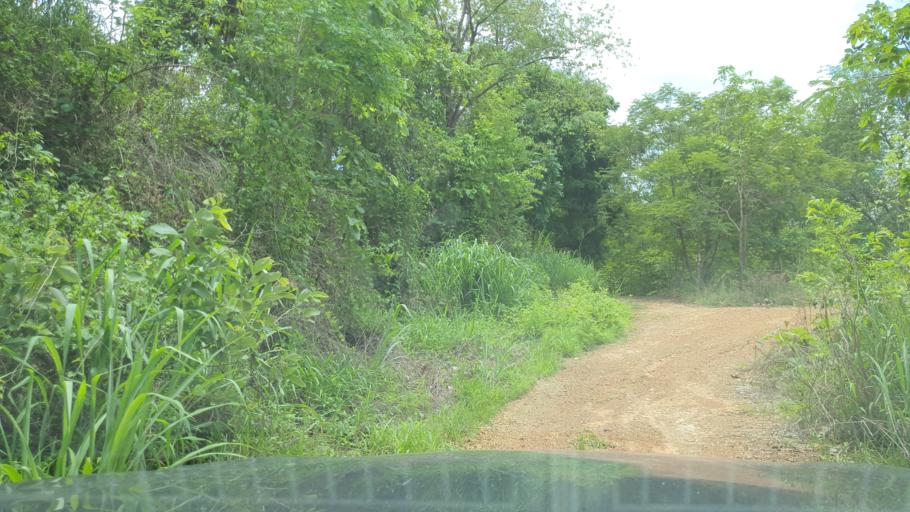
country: TH
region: Chiang Mai
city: San Sai
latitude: 18.9244
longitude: 99.0566
